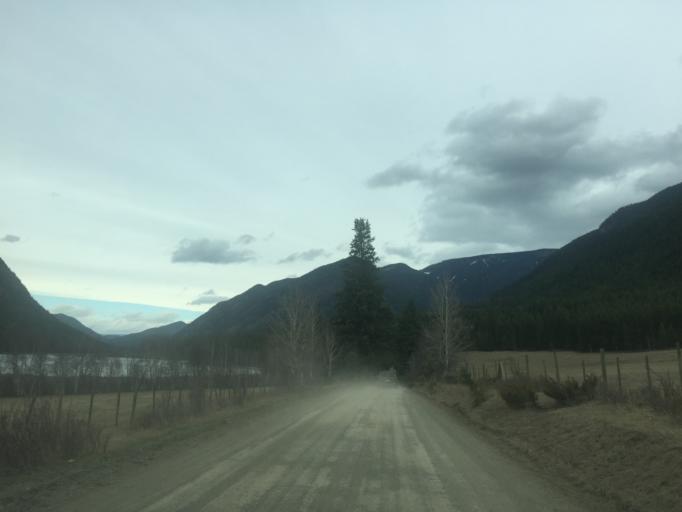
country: CA
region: British Columbia
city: Chase
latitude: 51.3811
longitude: -120.1279
